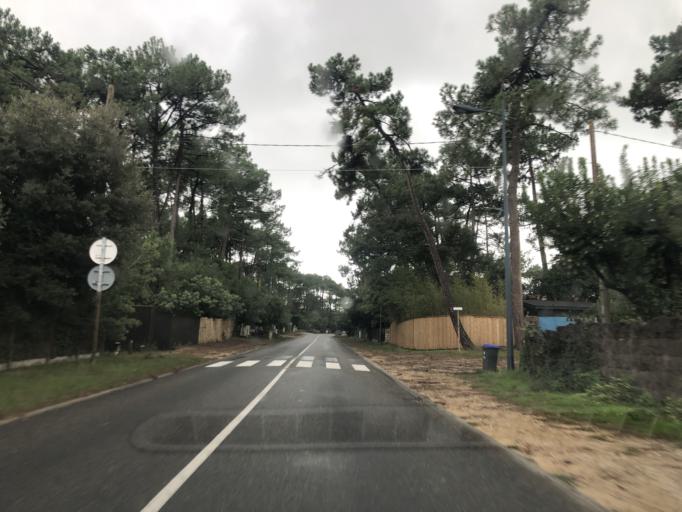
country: FR
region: Aquitaine
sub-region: Departement de la Gironde
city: Arcachon
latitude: 44.6965
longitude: -1.2322
